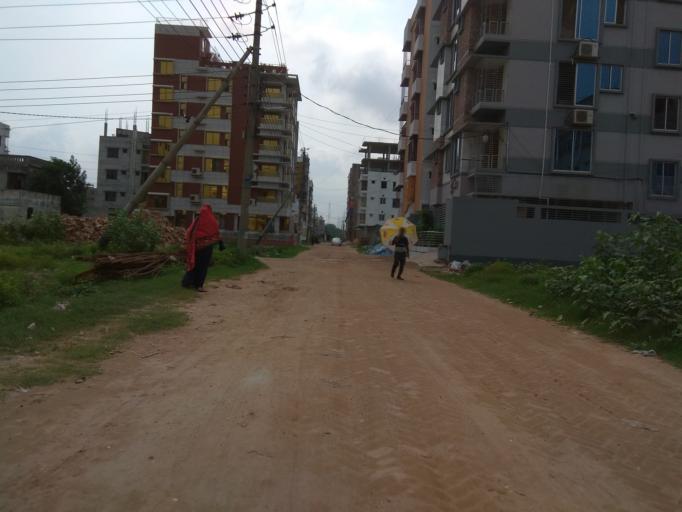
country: BD
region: Dhaka
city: Tungi
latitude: 23.8308
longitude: 90.3511
